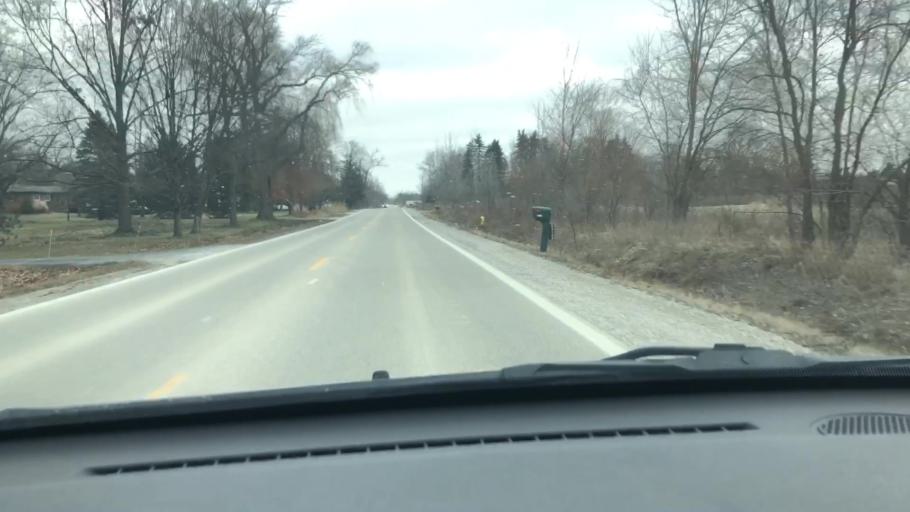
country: US
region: Michigan
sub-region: Macomb County
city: Romeo
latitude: 42.7365
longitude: -83.0172
